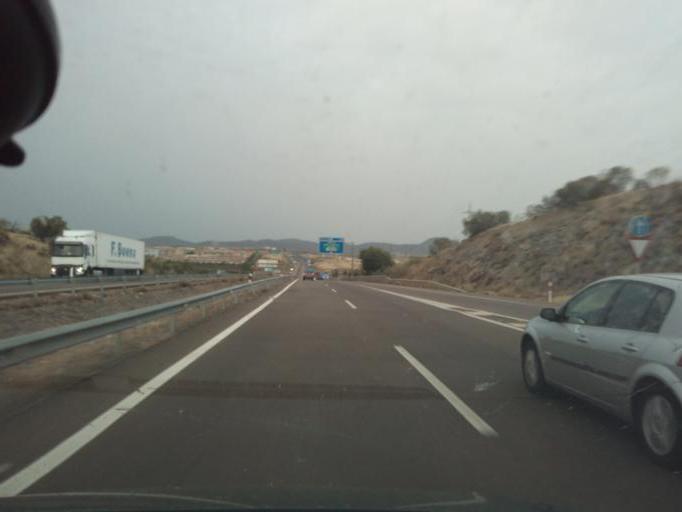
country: ES
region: Extremadura
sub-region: Provincia de Badajoz
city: Merida
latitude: 38.9357
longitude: -6.3654
